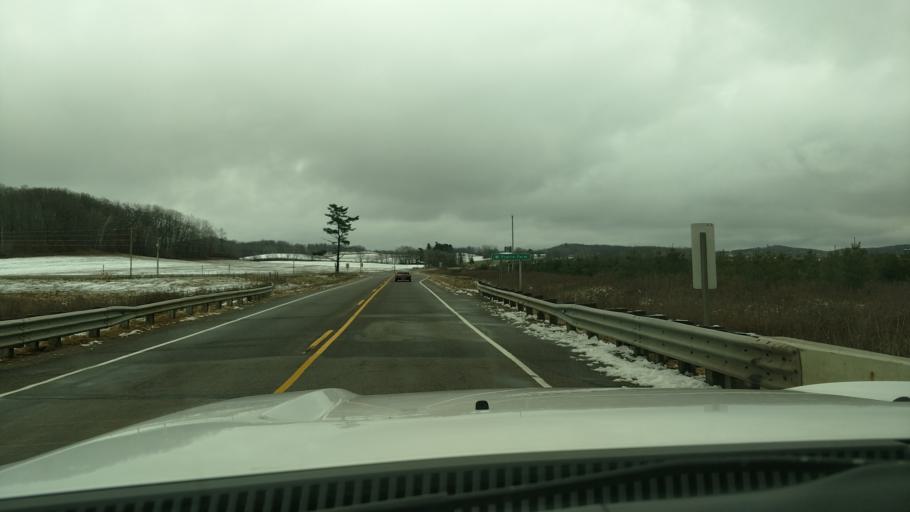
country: US
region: Wisconsin
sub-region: Dunn County
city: Boyceville
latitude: 45.1400
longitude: -91.9723
